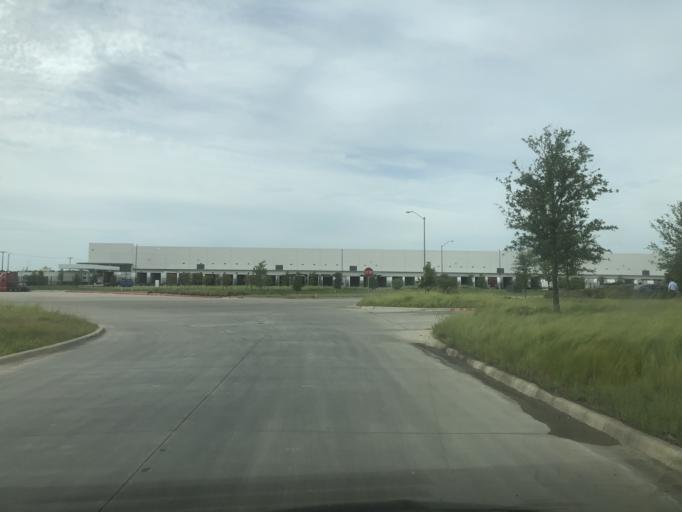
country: US
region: Texas
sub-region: Dallas County
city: Grand Prairie
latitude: 32.7732
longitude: -96.9963
